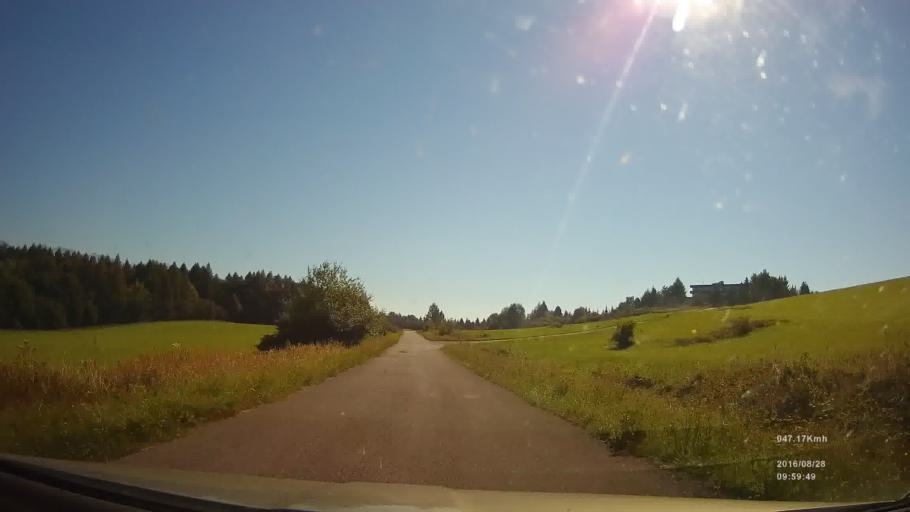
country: SK
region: Zilinsky
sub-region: Okres Liptovsky Mikulas
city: Liptovsky Mikulas
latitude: 49.1114
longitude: 19.4884
